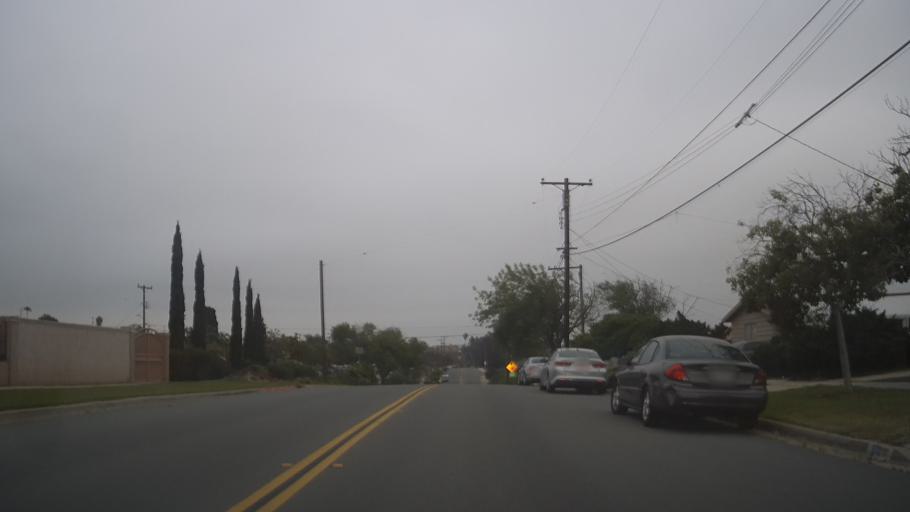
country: US
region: California
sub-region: San Diego County
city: Bonita
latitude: 32.6245
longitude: -117.0485
